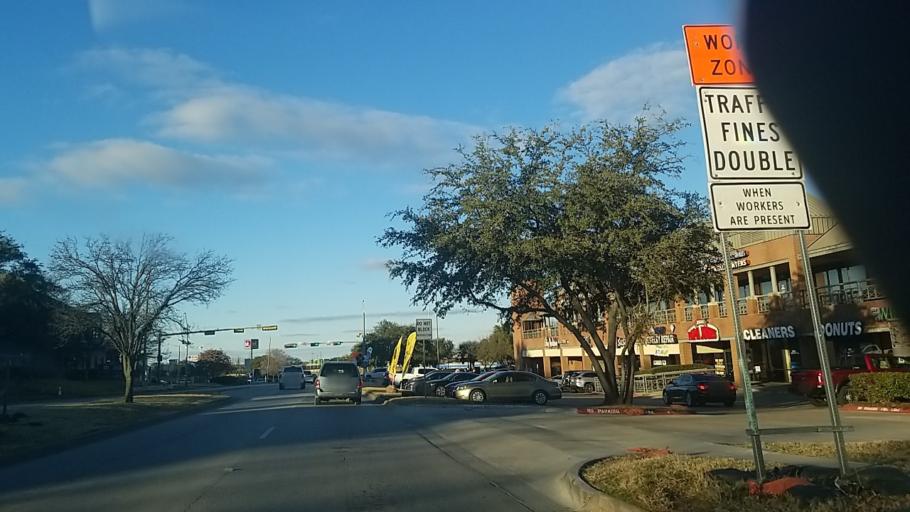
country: US
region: Texas
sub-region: Denton County
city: Denton
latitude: 33.1840
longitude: -97.1087
